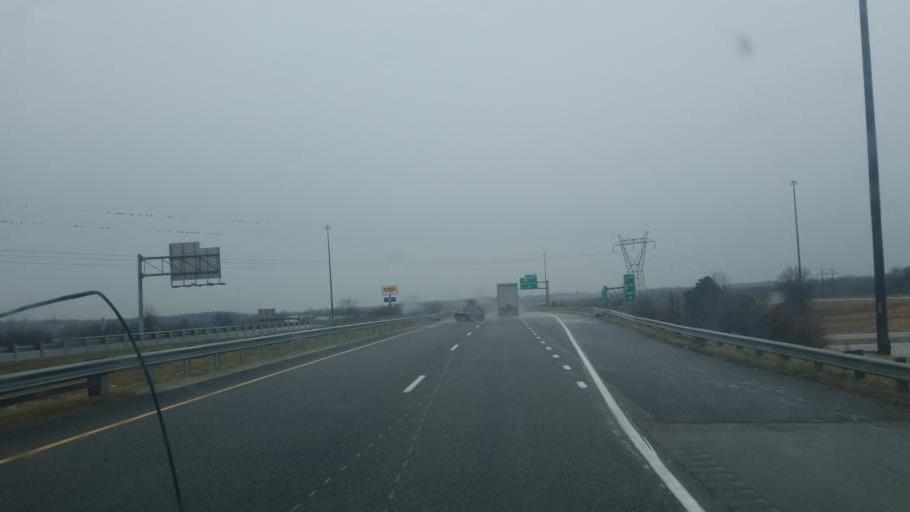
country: US
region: Ohio
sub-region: Preble County
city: New Paris
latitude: 39.8325
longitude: -84.8159
